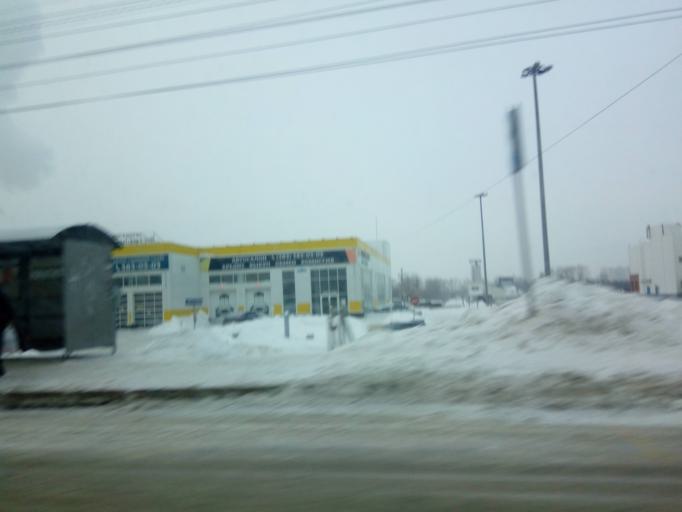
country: RU
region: Novosibirsk
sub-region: Novosibirskiy Rayon
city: Novosibirsk
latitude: 55.0097
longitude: 82.8744
